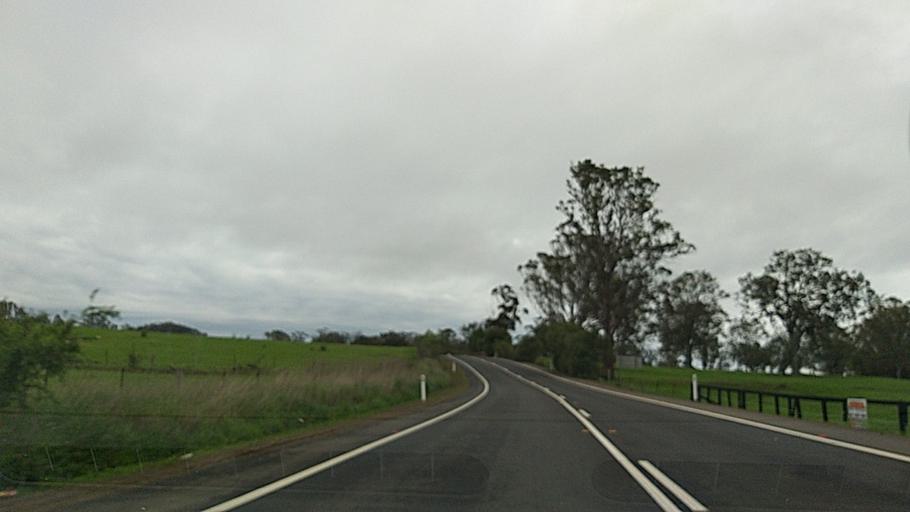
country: AU
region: New South Wales
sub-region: Wollondilly
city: Douglas Park
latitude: -34.1343
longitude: 150.7103
